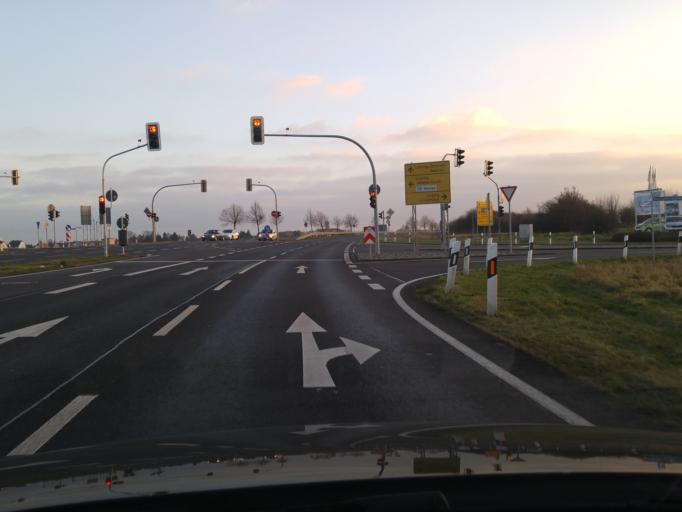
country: DE
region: Saxony
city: Rackwitz
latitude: 51.3943
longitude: 12.3431
